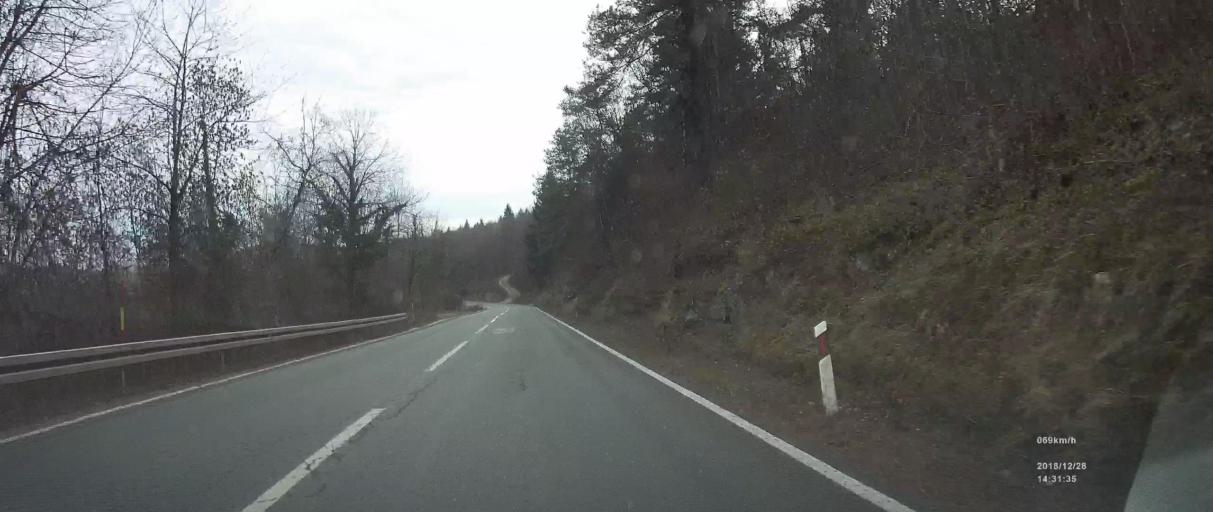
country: HR
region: Primorsko-Goranska
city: Vrbovsko
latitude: 45.4164
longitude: 15.1449
